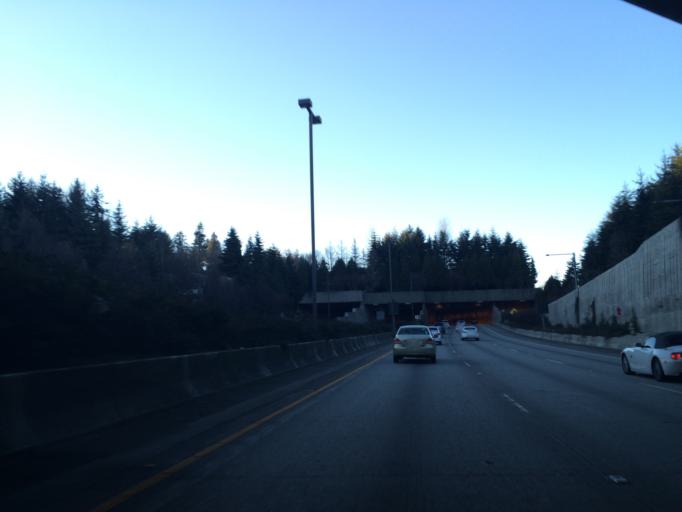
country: US
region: Washington
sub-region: King County
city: Mercer Island
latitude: 47.5901
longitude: -122.2376
